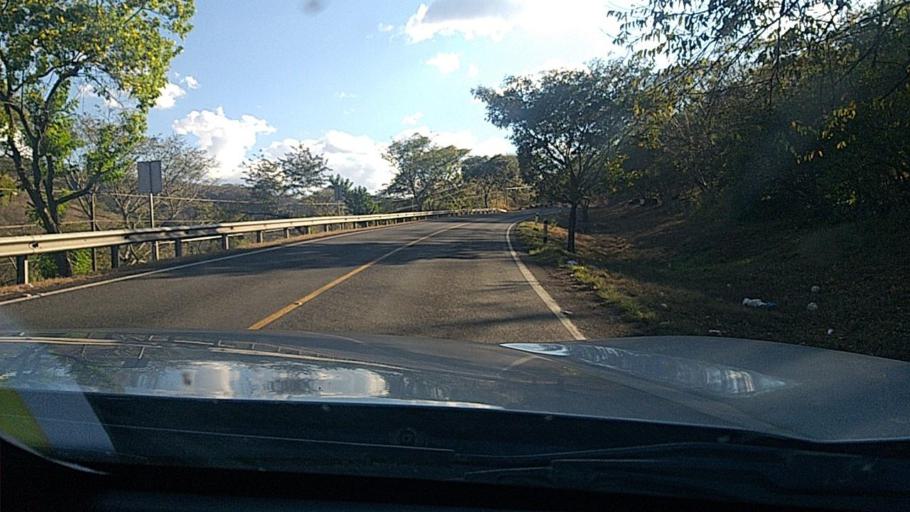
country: NI
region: Esteli
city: Condega
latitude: 13.2822
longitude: -86.3457
